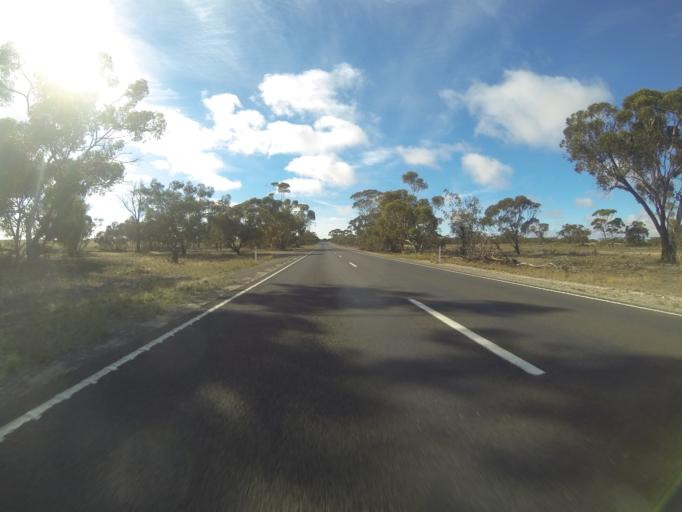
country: AU
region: South Australia
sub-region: Loxton Waikerie
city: Loxton
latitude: -35.2477
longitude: 141.0597
